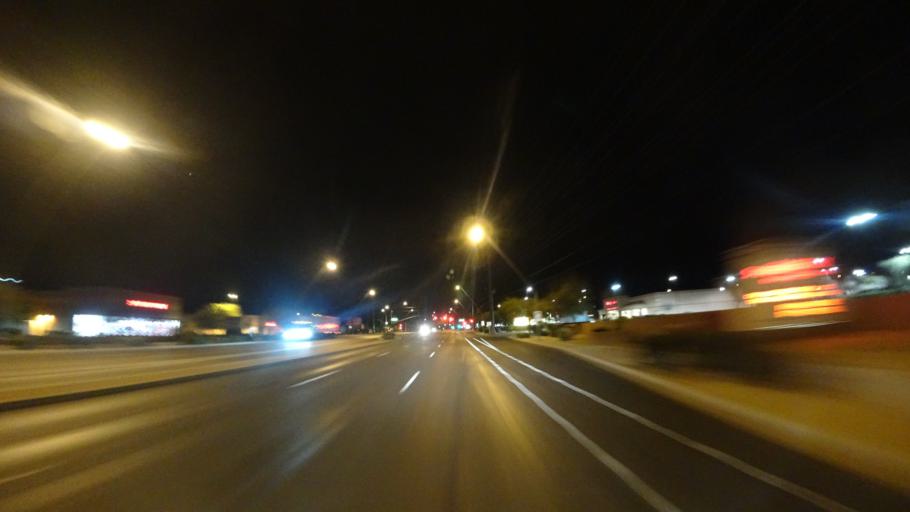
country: US
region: Arizona
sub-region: Pinal County
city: Apache Junction
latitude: 33.4499
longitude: -111.6840
